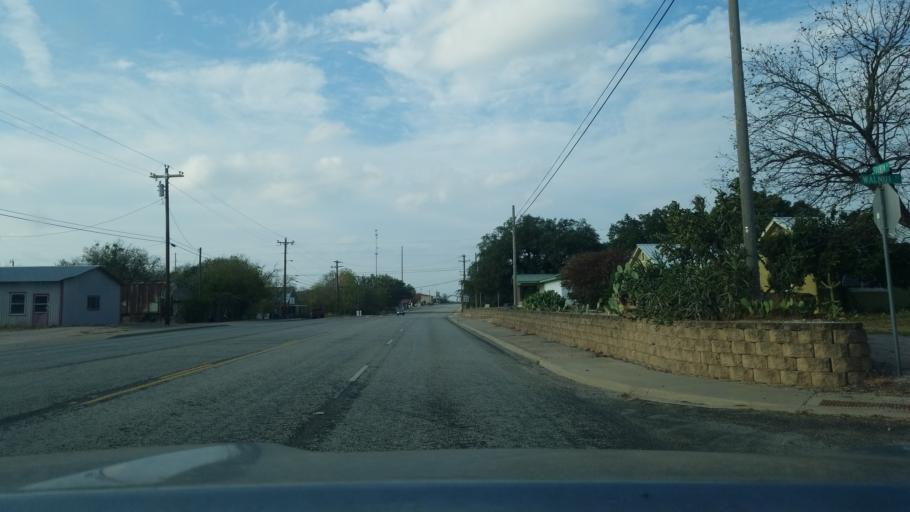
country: US
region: Texas
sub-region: Lampasas County
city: Lampasas
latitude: 31.2122
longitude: -98.3912
